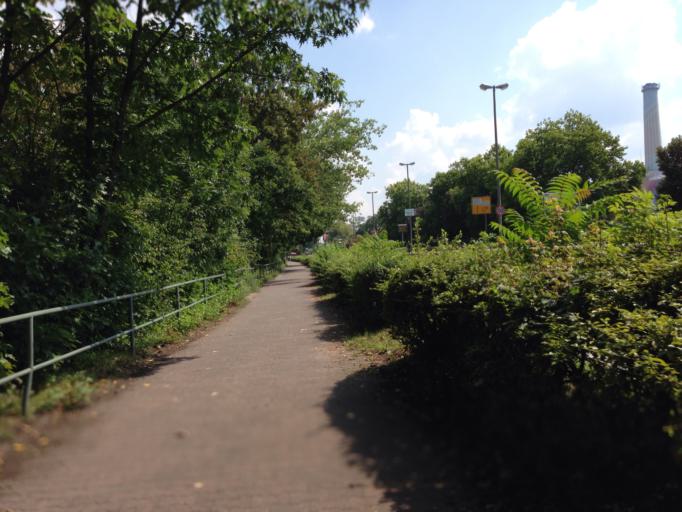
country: DE
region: Hesse
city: Niederrad
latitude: 50.0881
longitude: 8.6223
